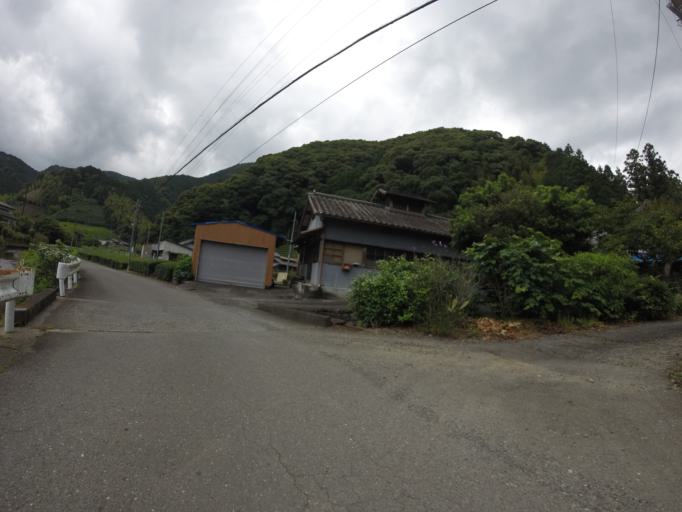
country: JP
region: Shizuoka
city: Shizuoka-shi
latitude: 35.0137
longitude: 138.3112
